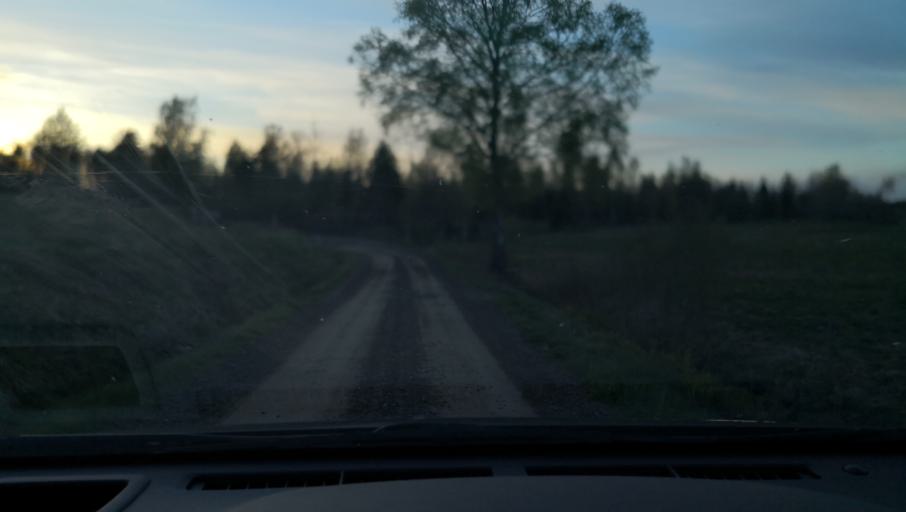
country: SE
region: OErebro
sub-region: Askersunds Kommun
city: Asbro
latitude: 58.9810
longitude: 14.9479
